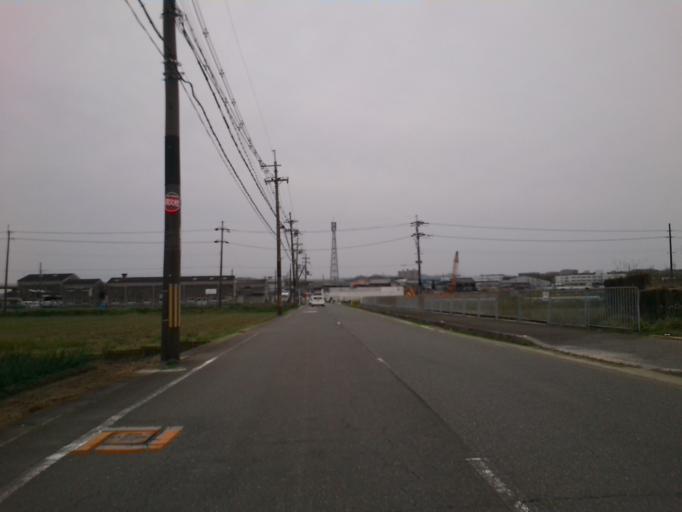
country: JP
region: Kyoto
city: Yawata
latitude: 34.8561
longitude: 135.7287
